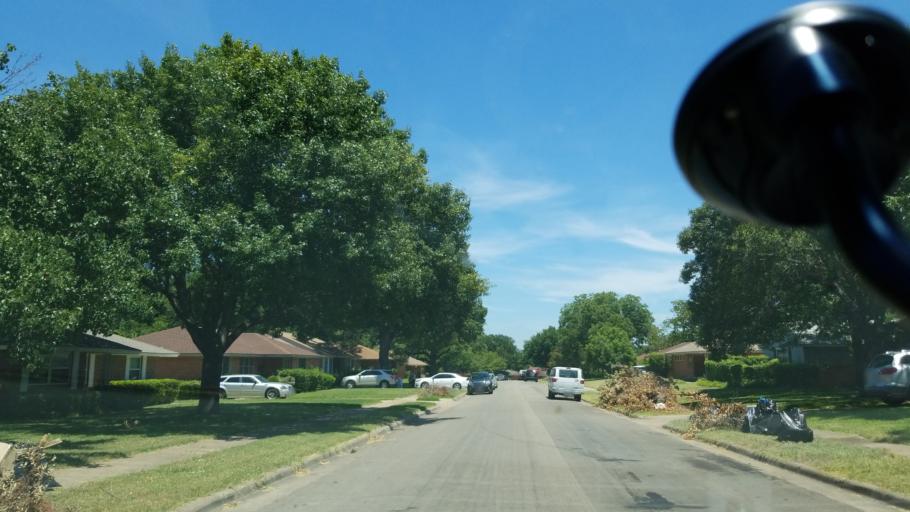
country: US
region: Texas
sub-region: Dallas County
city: Cockrell Hill
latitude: 32.6898
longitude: -96.8372
